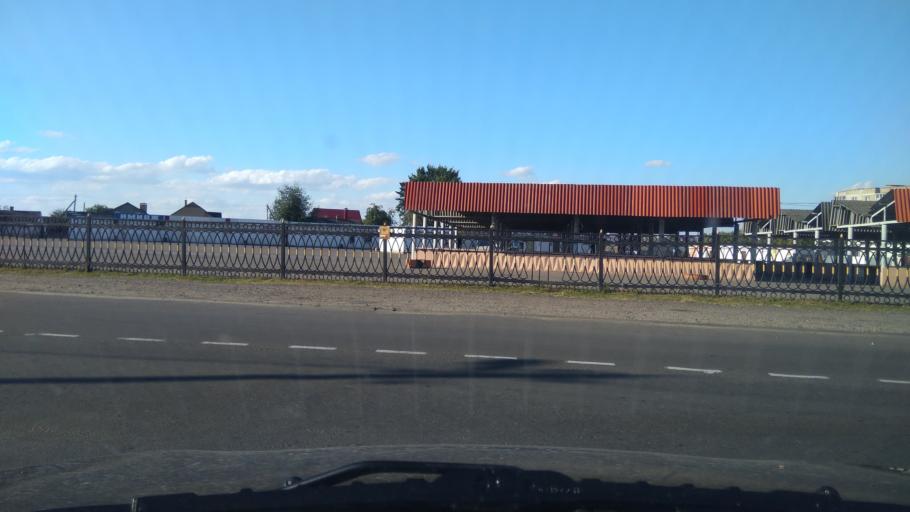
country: BY
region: Brest
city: Byaroza
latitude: 52.5404
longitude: 24.9780
